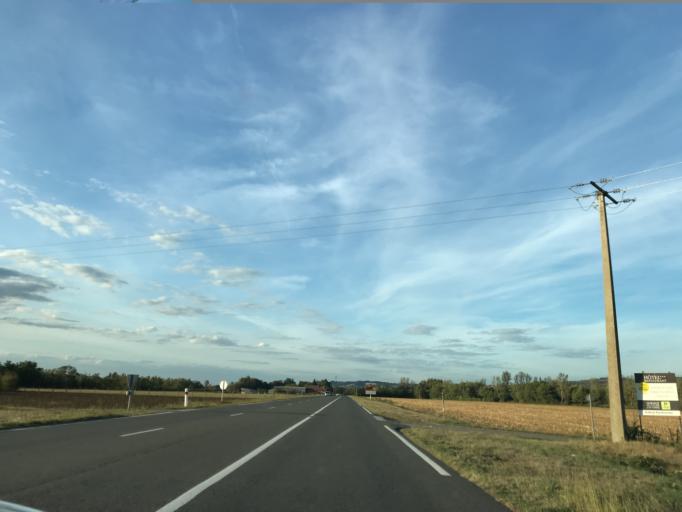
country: FR
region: Auvergne
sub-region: Departement de l'Allier
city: Saint-Yorre
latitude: 46.0323
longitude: 3.4767
